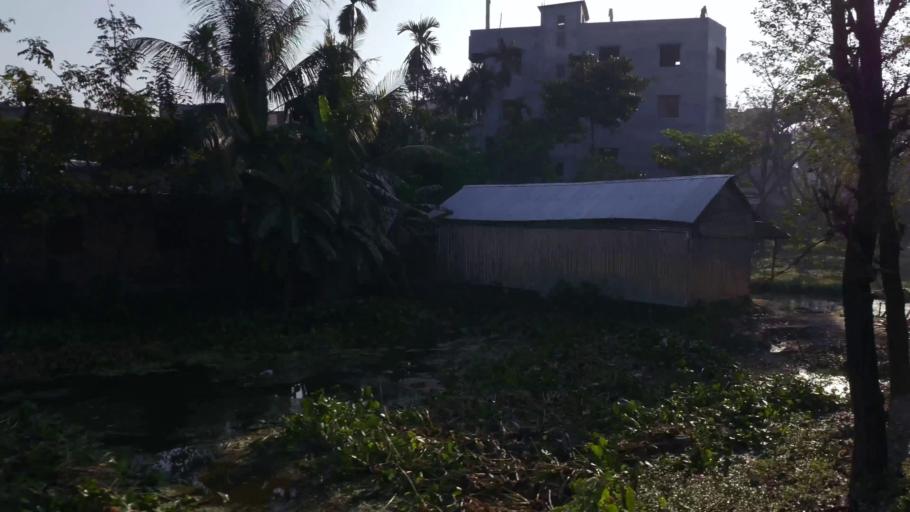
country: BD
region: Dhaka
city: Jamalpur
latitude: 24.9021
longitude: 89.9758
